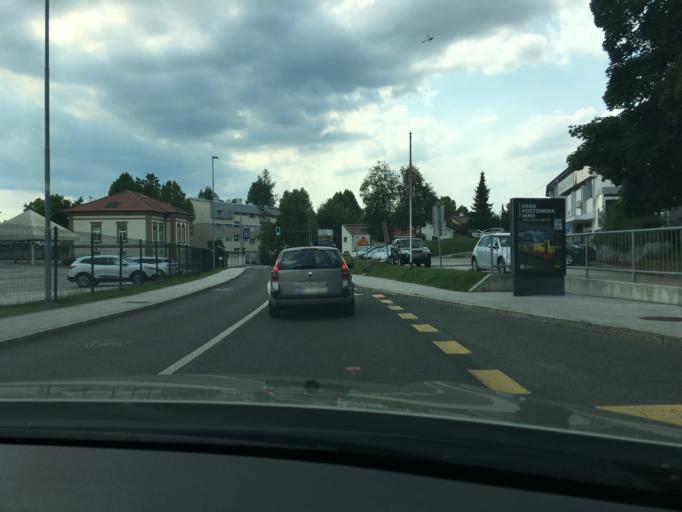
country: SI
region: Novo Mesto
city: Novo Mesto
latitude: 45.8001
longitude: 15.1746
